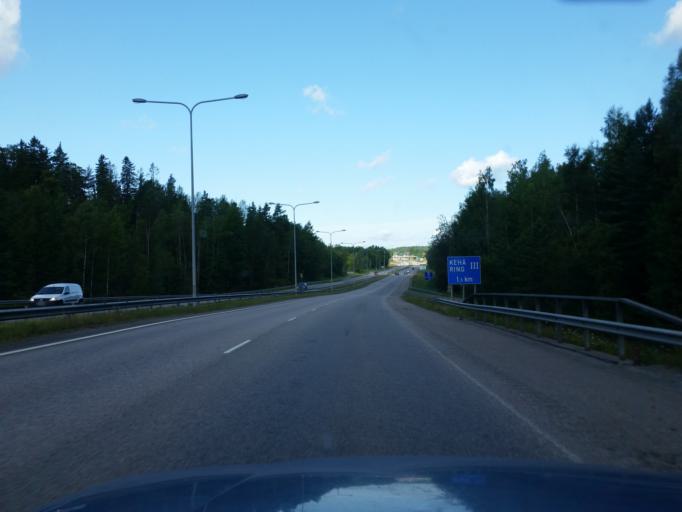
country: FI
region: Uusimaa
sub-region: Helsinki
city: Espoo
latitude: 60.2107
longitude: 24.6795
